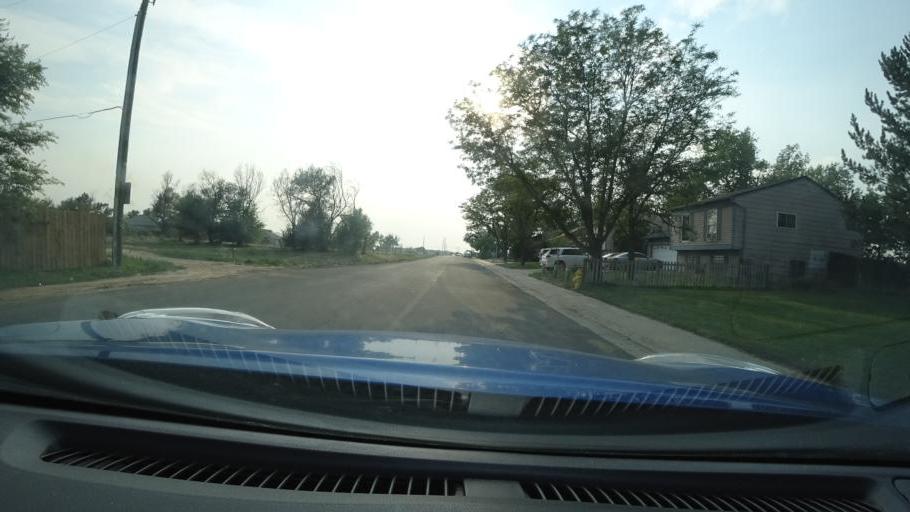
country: US
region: Colorado
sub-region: Adams County
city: Aurora
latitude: 39.7474
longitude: -104.7692
